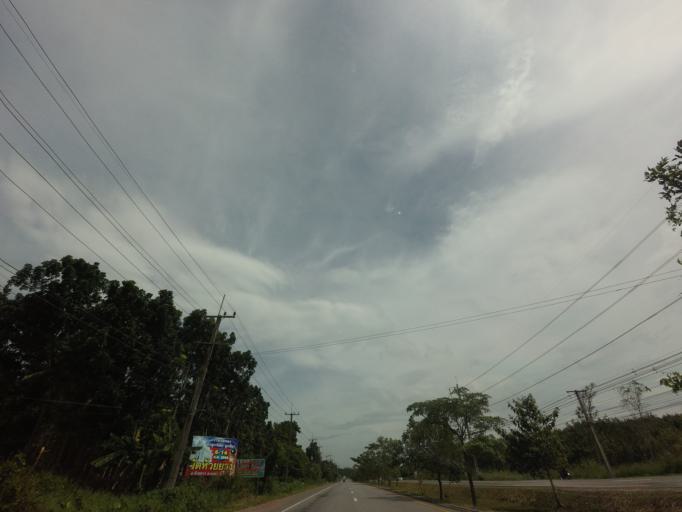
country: TH
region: Rayong
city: Klaeng
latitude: 12.6957
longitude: 101.5390
